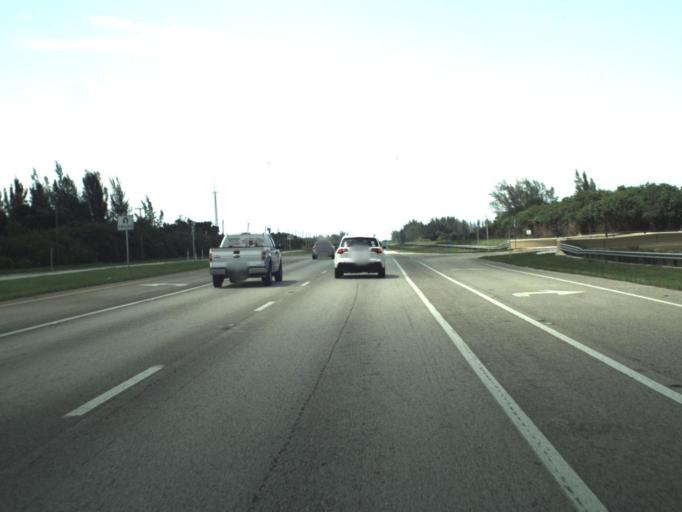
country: US
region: Florida
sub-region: Palm Beach County
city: Villages of Oriole
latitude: 26.4593
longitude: -80.2044
